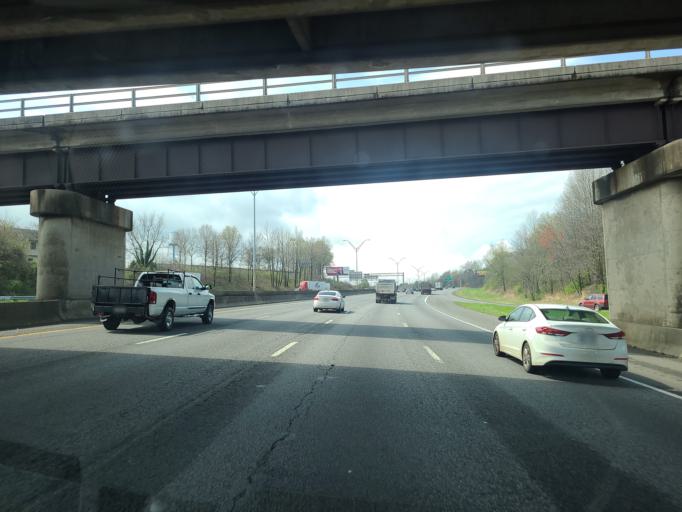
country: US
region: North Carolina
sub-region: Mecklenburg County
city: Charlotte
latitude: 35.2613
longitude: -80.8801
